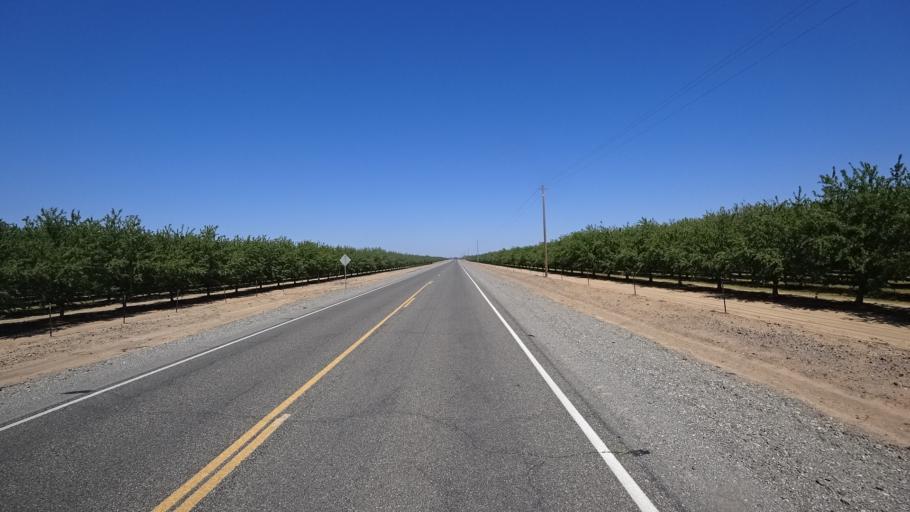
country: US
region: California
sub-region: Glenn County
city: Orland
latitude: 39.6694
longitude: -122.1970
